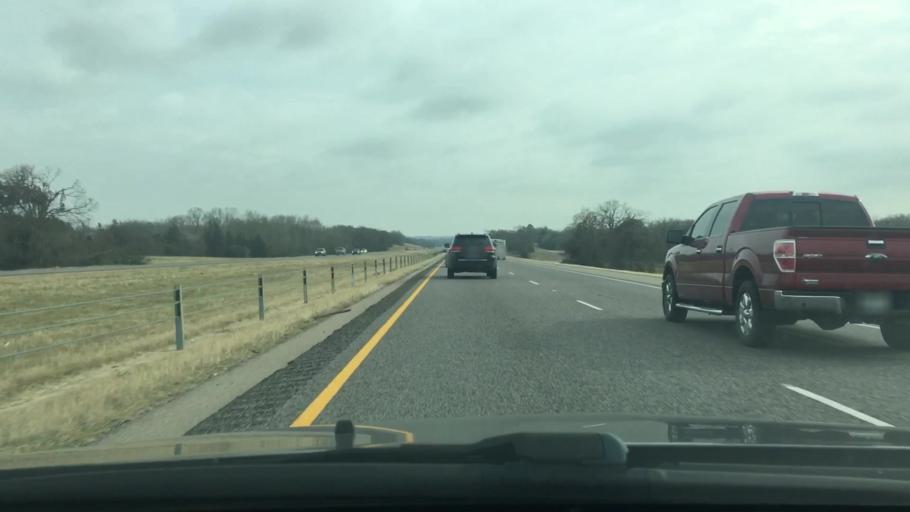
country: US
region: Texas
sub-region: Leon County
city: Buffalo
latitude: 31.5243
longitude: -96.1124
